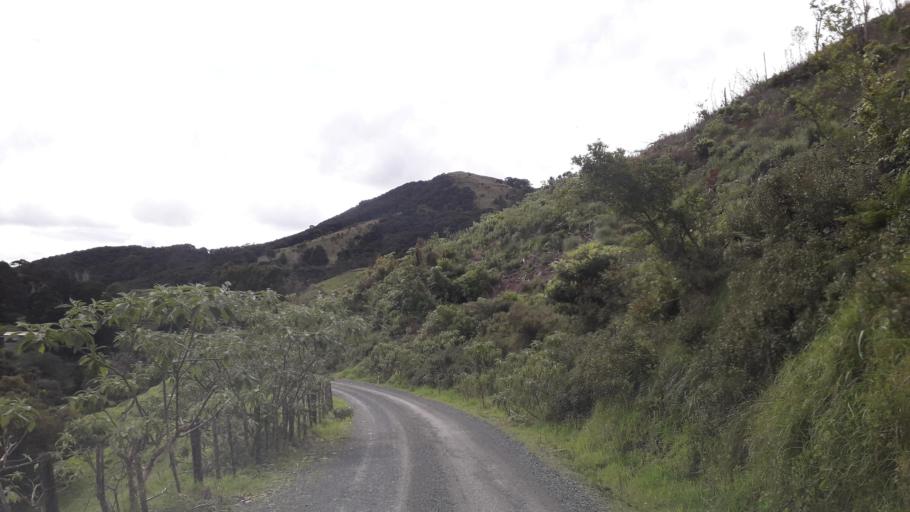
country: NZ
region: Northland
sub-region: Far North District
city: Taipa
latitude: -35.0957
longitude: 173.5383
